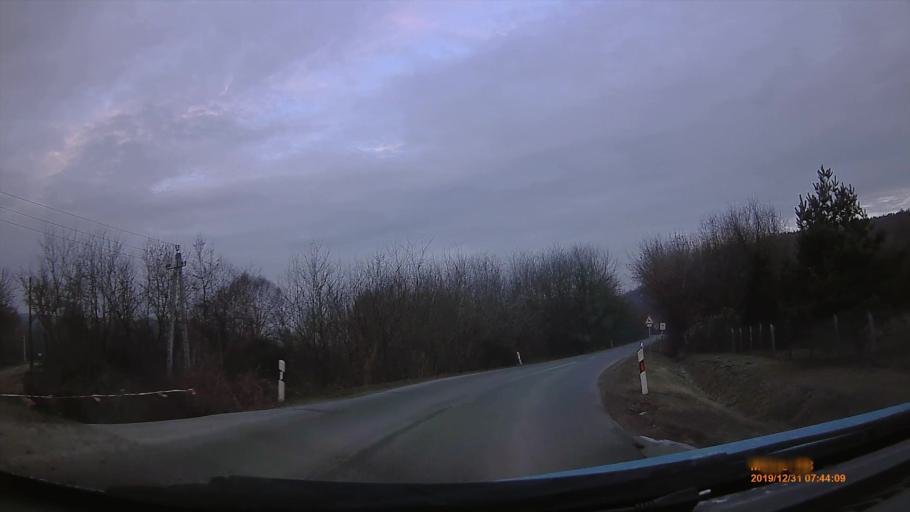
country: HU
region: Heves
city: Recsk
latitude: 47.9257
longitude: 20.1482
